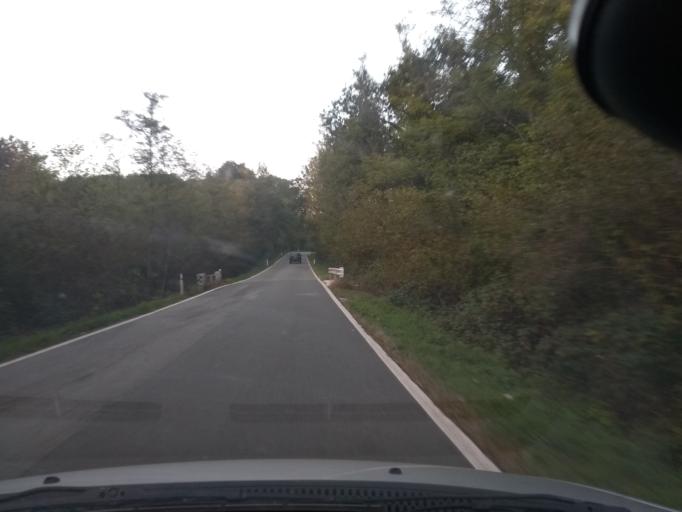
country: IT
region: Piedmont
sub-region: Provincia di Torino
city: La Cassa
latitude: 45.2002
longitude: 7.5141
